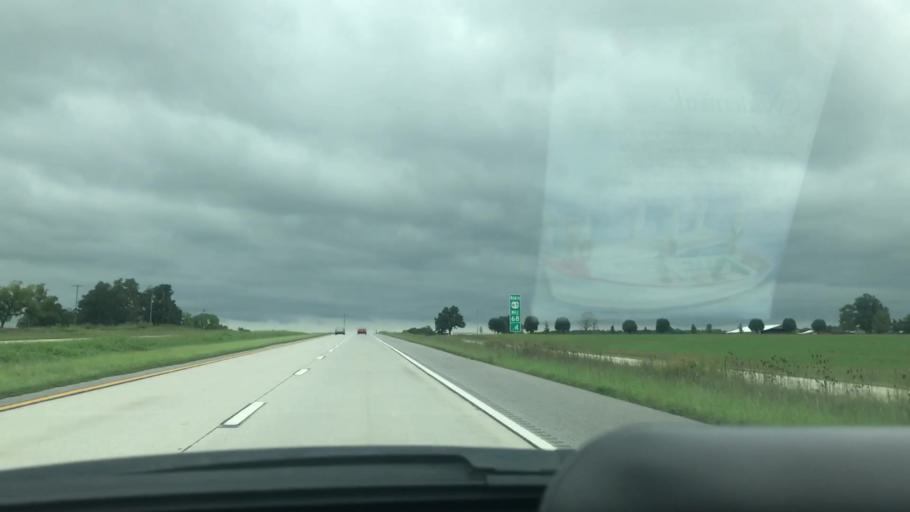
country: US
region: Missouri
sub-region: Greene County
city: Fair Grove
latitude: 37.4340
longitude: -93.1446
